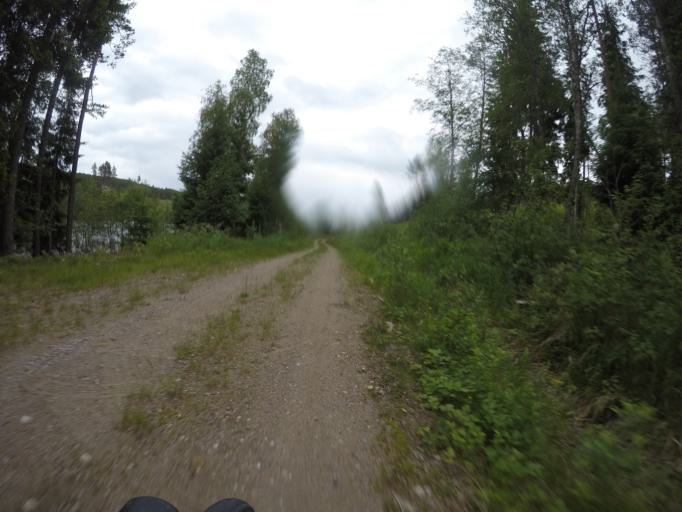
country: SE
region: Dalarna
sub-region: Ludvika Kommun
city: Abborrberget
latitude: 60.0500
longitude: 14.5887
